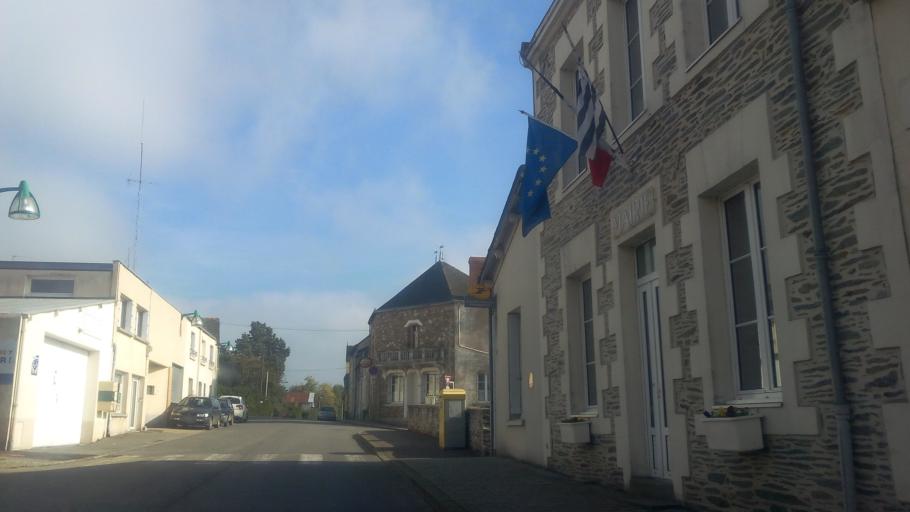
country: FR
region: Pays de la Loire
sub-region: Departement de la Loire-Atlantique
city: Conquereuil
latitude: 47.6248
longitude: -1.7504
